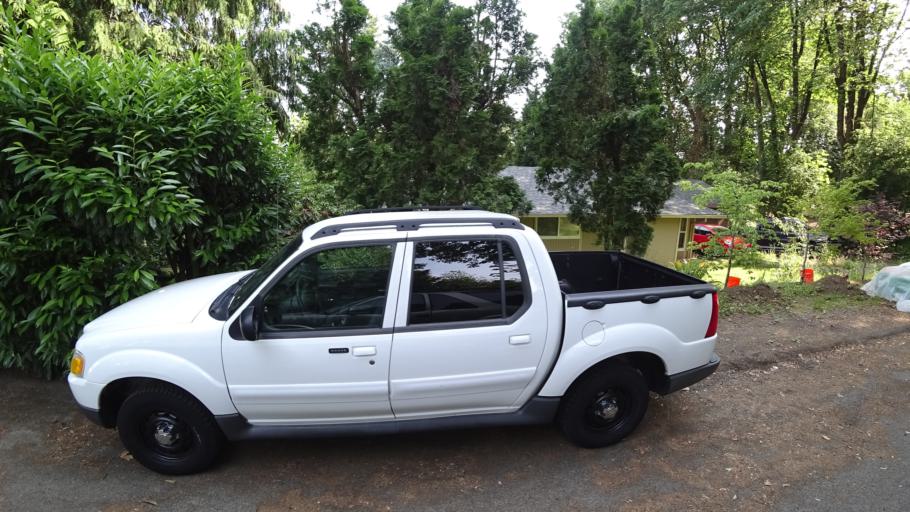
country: US
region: Oregon
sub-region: Washington County
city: Garden Home-Whitford
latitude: 45.4626
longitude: -122.7099
